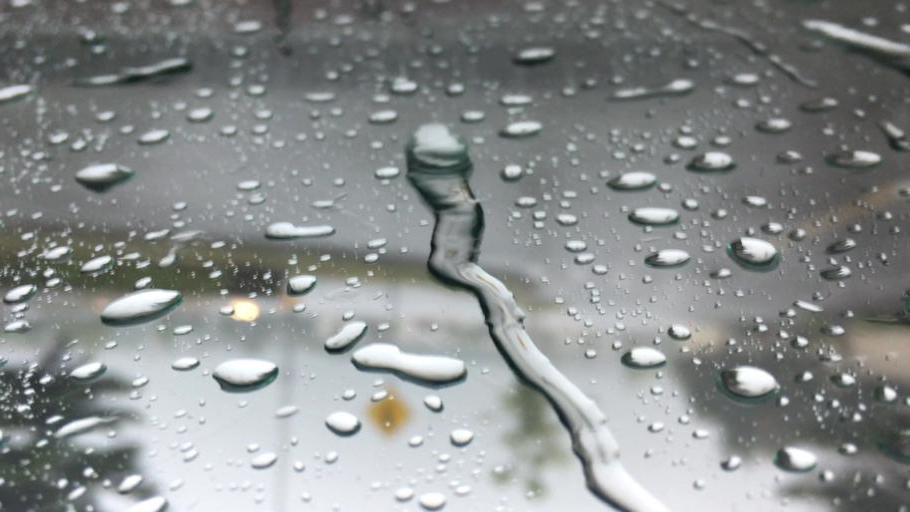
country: US
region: Massachusetts
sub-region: Middlesex County
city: Burlington
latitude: 42.4852
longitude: -71.2136
